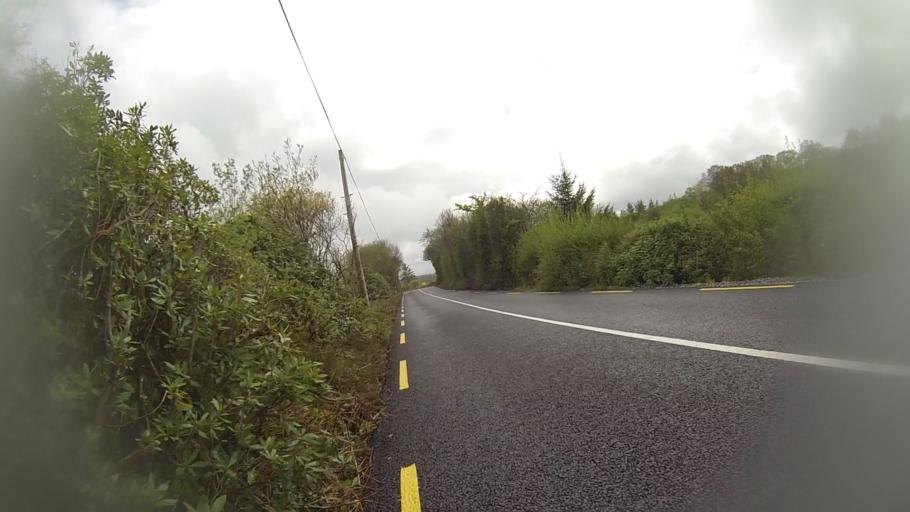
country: IE
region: Munster
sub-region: Ciarrai
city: Killorglin
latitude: 51.8478
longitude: -9.8894
